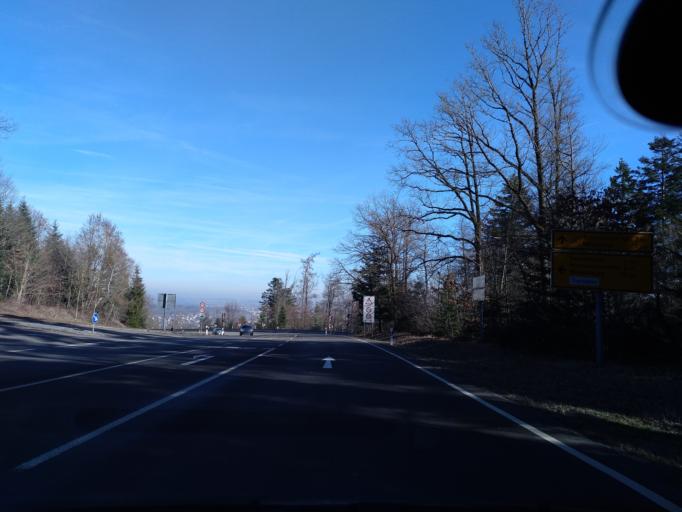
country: DE
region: Baden-Wuerttemberg
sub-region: Regierungsbezirk Stuttgart
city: Michelfeld
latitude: 49.0886
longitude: 9.6467
